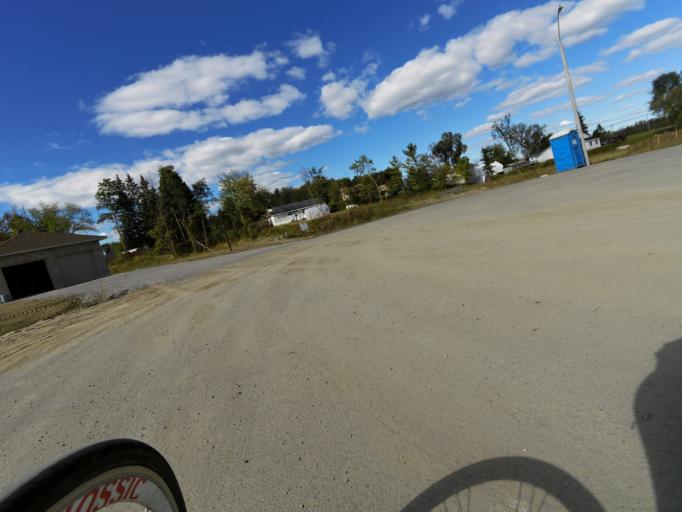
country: CA
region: Ontario
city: Bells Corners
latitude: 45.1567
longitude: -75.6521
